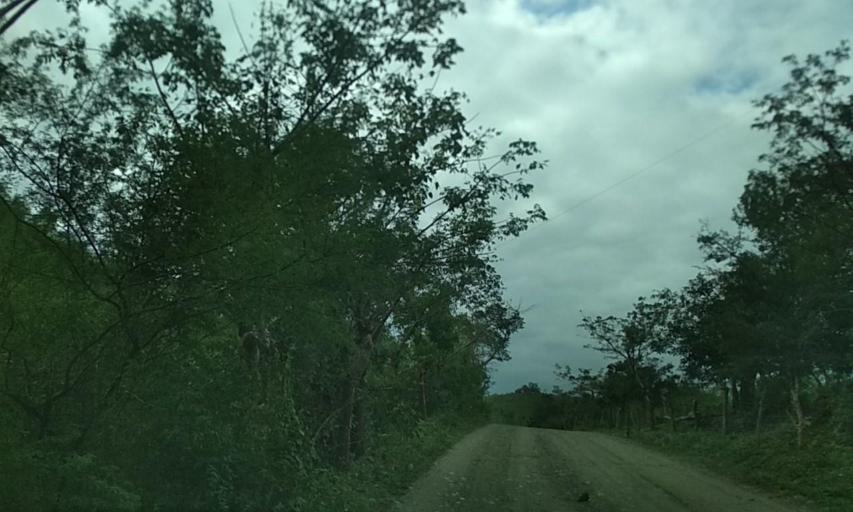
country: MX
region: Veracruz
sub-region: Papantla
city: Residencial Tajin
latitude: 20.6142
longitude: -97.3601
